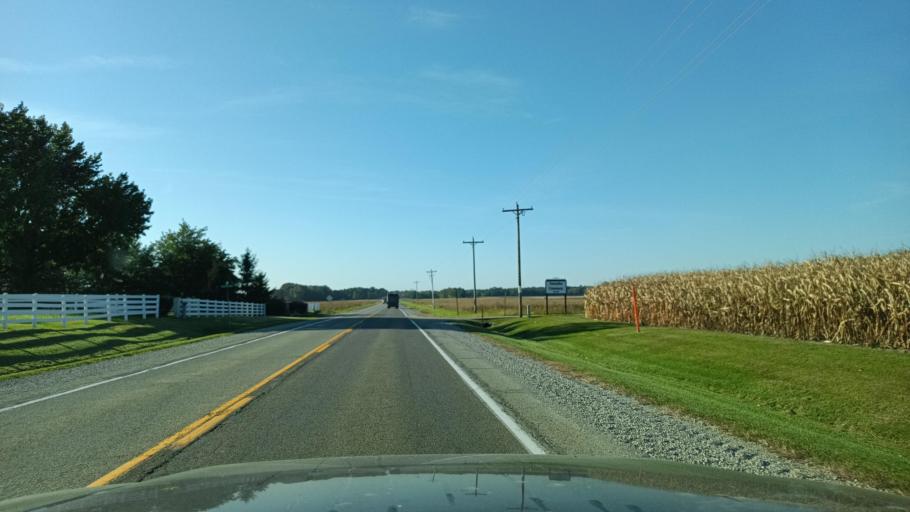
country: US
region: Illinois
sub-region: Clark County
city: Marshall
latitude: 39.4615
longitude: -87.6821
